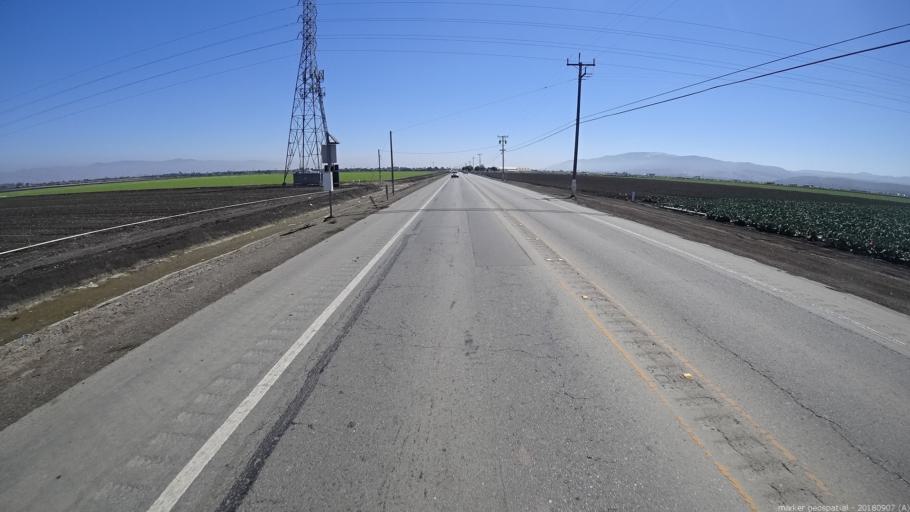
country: US
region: California
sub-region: Monterey County
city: Boronda
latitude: 36.6745
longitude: -121.6986
